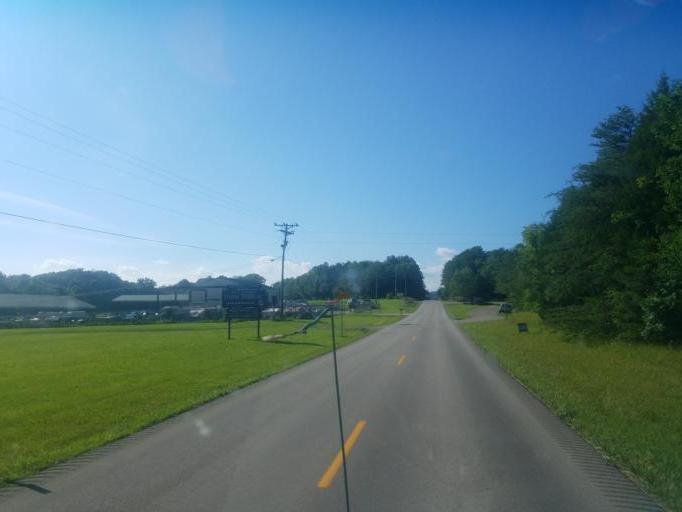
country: US
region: Kentucky
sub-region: Edmonson County
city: Brownsville
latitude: 37.3334
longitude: -86.1248
